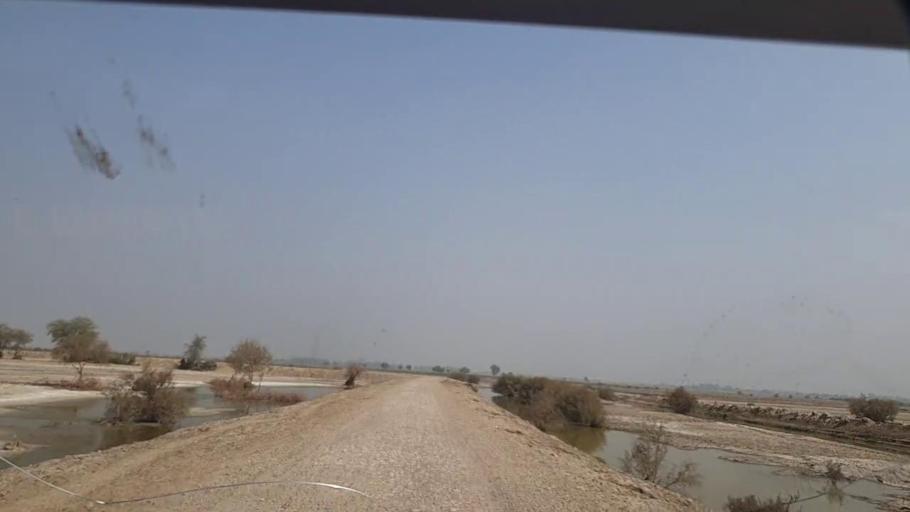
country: PK
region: Sindh
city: Shikarpur
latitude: 28.0396
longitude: 68.6458
